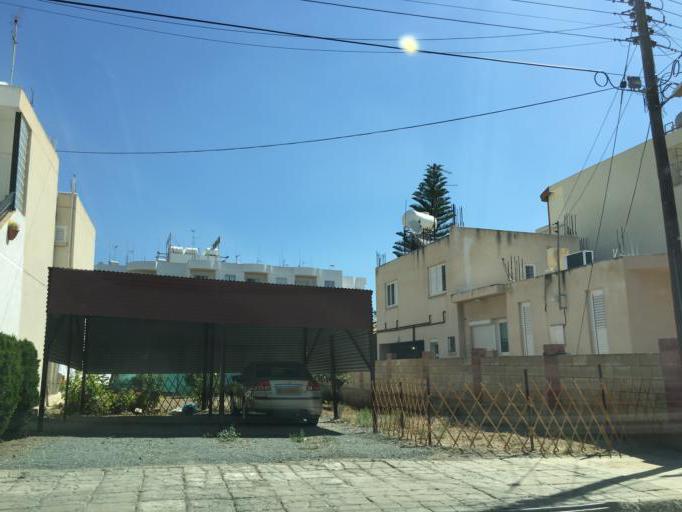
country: CY
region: Lefkosia
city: Nicosia
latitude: 35.1563
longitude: 33.3138
